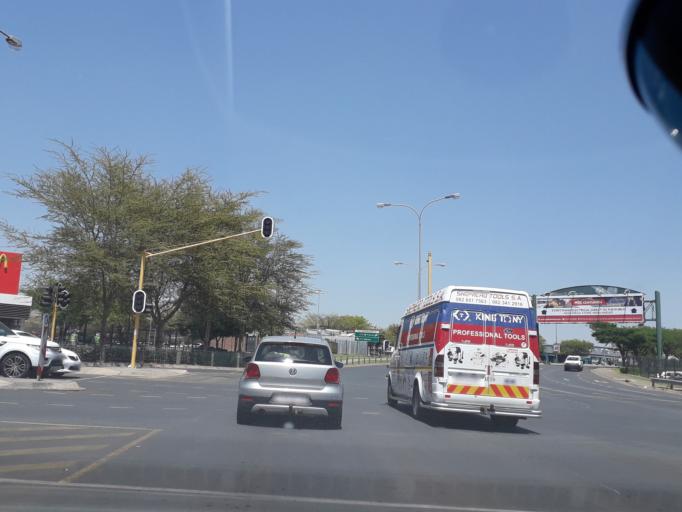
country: ZA
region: Gauteng
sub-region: City of Tshwane Metropolitan Municipality
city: Centurion
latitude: -25.8769
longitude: 28.1638
